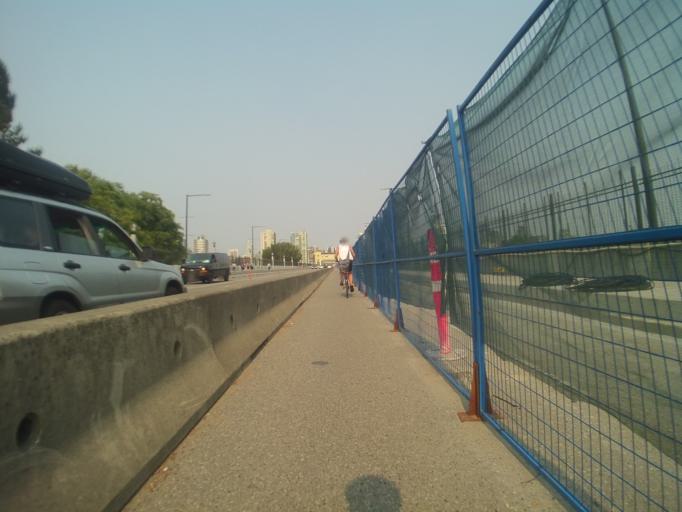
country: CA
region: British Columbia
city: West End
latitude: 49.2741
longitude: -123.1413
